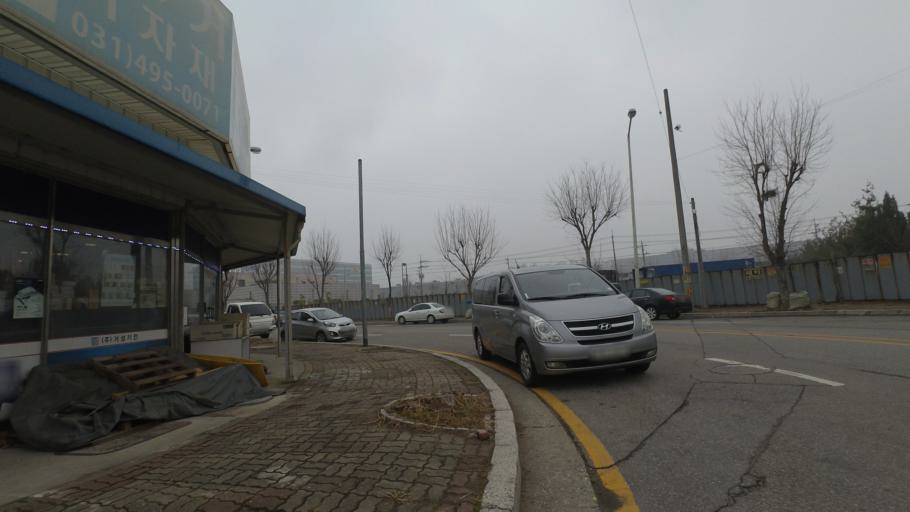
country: KR
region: Chungcheongnam-do
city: Tangjin
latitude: 36.9739
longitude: 126.8443
